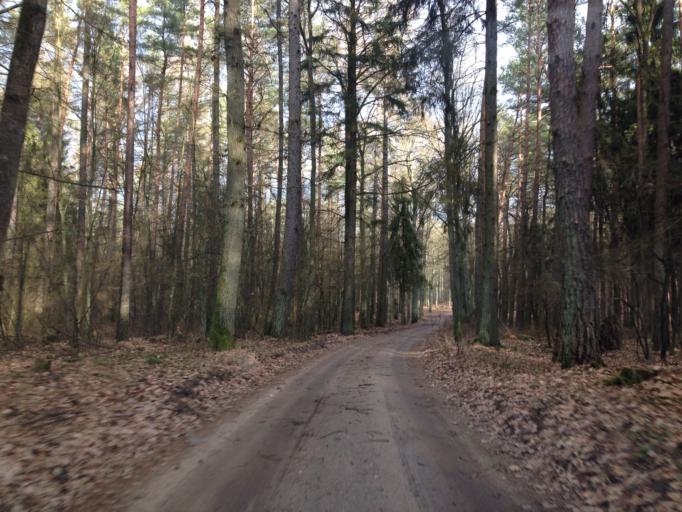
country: PL
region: Kujawsko-Pomorskie
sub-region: Powiat brodnicki
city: Gorzno
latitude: 53.2092
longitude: 19.6805
